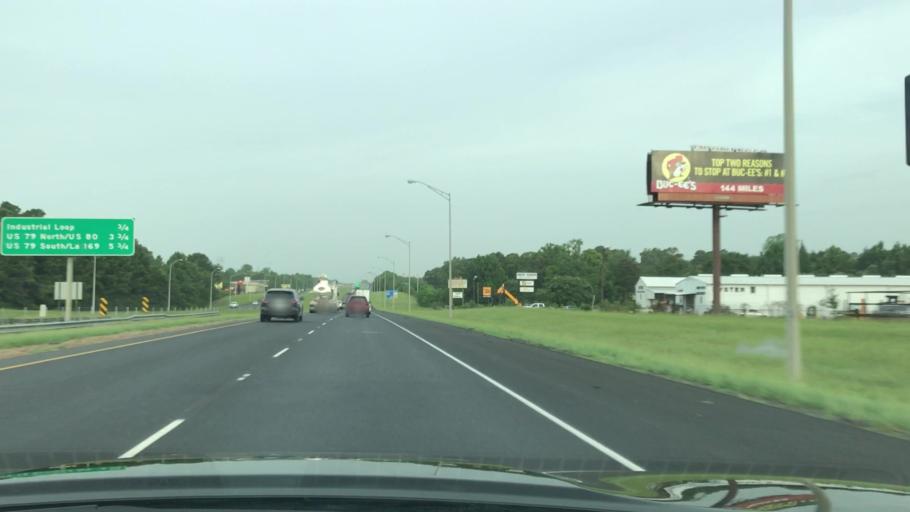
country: US
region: Louisiana
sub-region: Caddo Parish
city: Greenwood
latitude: 32.4497
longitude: -93.8851
